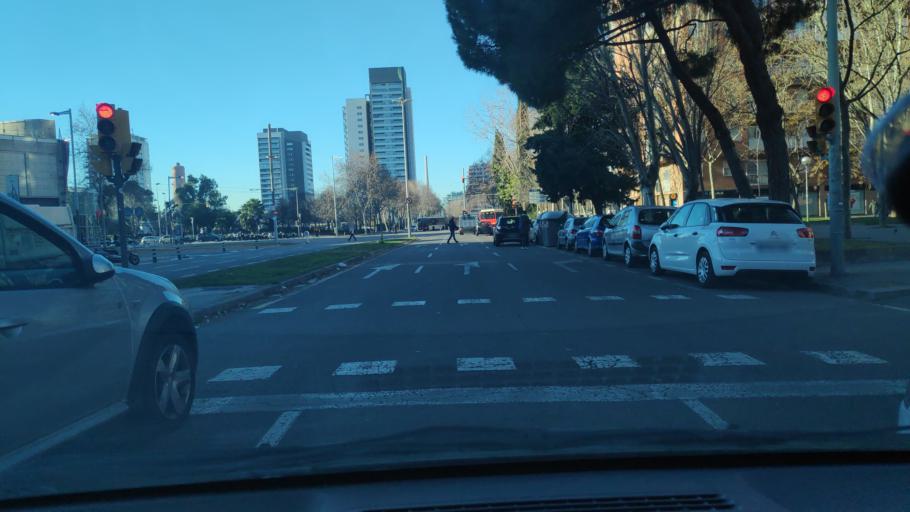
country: ES
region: Catalonia
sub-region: Provincia de Barcelona
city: Sant Marti
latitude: 41.4108
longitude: 2.2150
